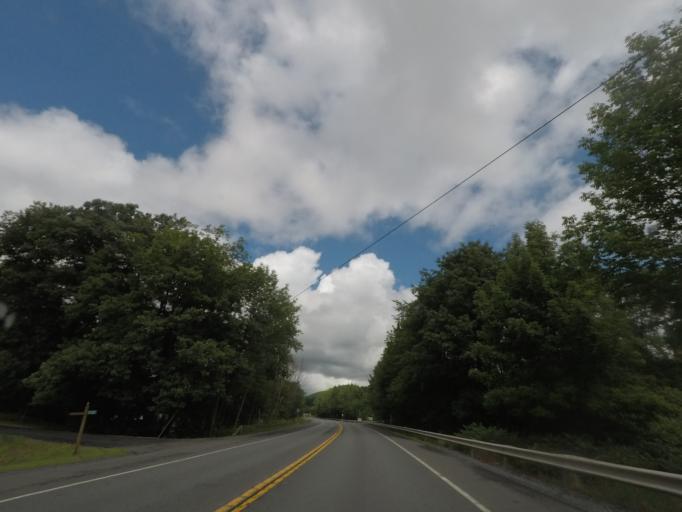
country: US
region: Massachusetts
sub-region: Berkshire County
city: Williamstown
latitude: 42.6332
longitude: -73.3588
